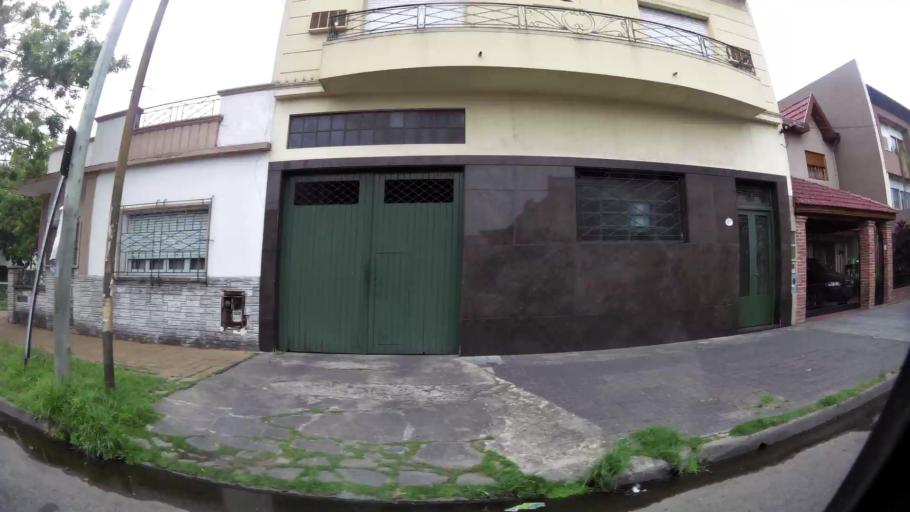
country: AR
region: Buenos Aires
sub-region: Partido de Lanus
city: Lanus
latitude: -34.6859
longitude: -58.3906
